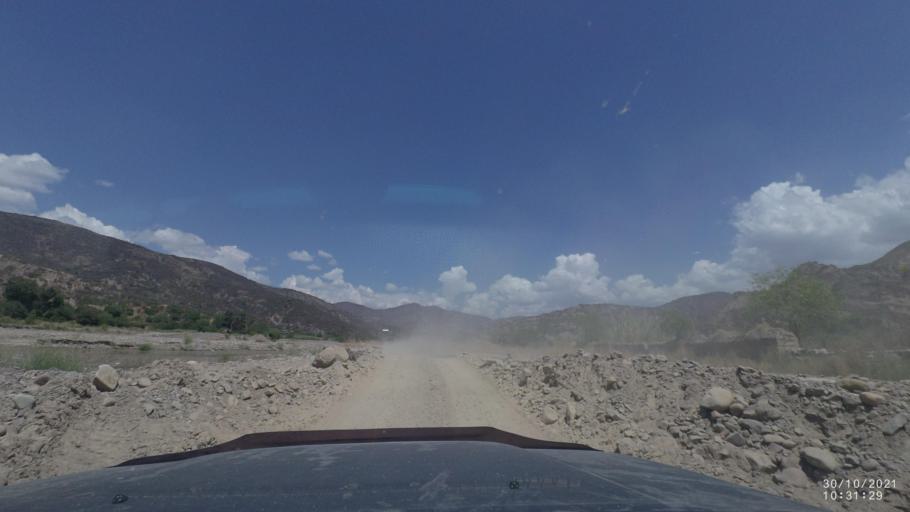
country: BO
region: Cochabamba
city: Sipe Sipe
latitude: -17.5473
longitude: -66.4076
